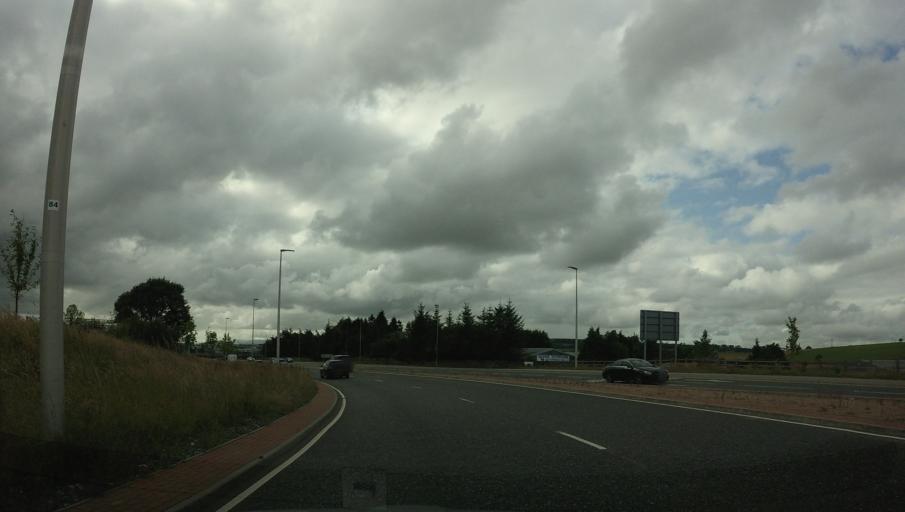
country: GB
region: Scotland
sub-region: Aberdeenshire
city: Westhill
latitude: 57.1476
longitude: -2.2452
